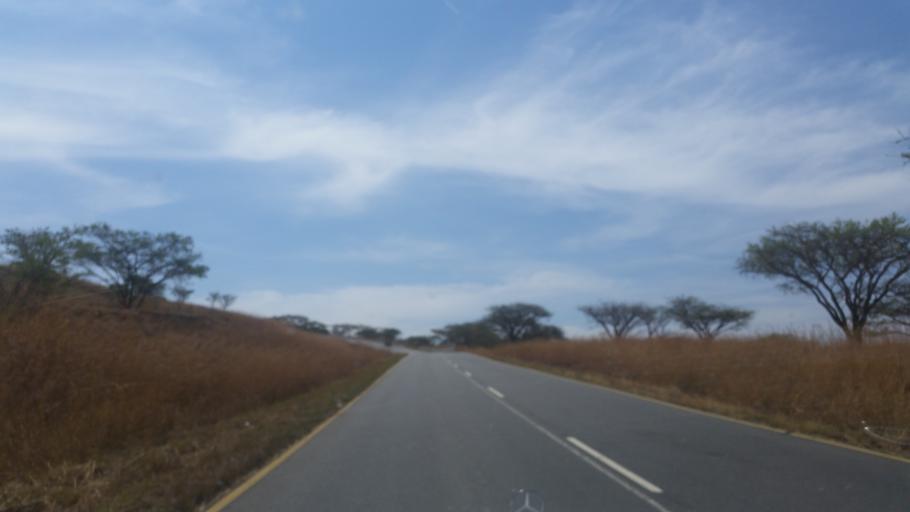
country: ZA
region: Orange Free State
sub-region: Thabo Mofutsanyana District Municipality
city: Phuthaditjhaba
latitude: -28.6174
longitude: 29.0828
